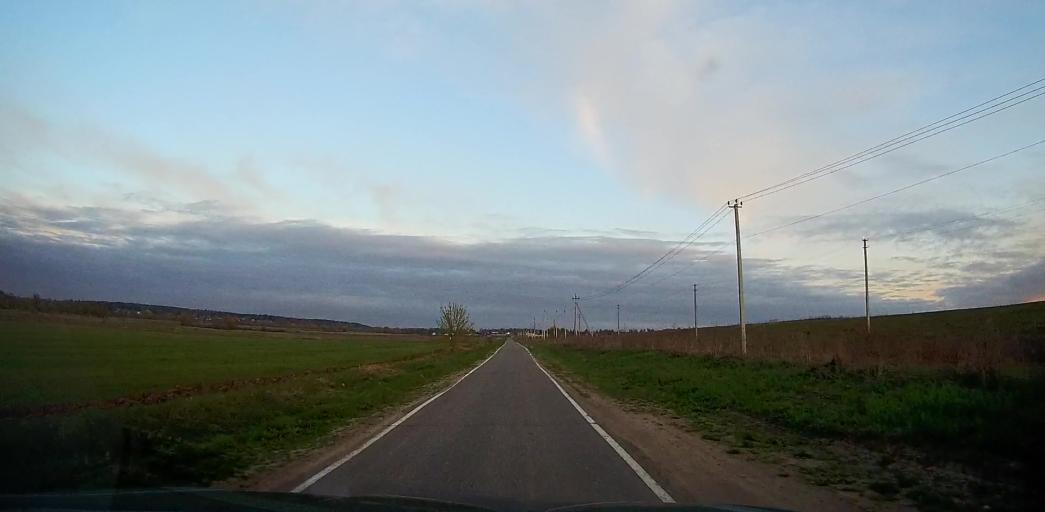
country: RU
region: Moskovskaya
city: Peski
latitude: 55.2243
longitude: 38.7359
